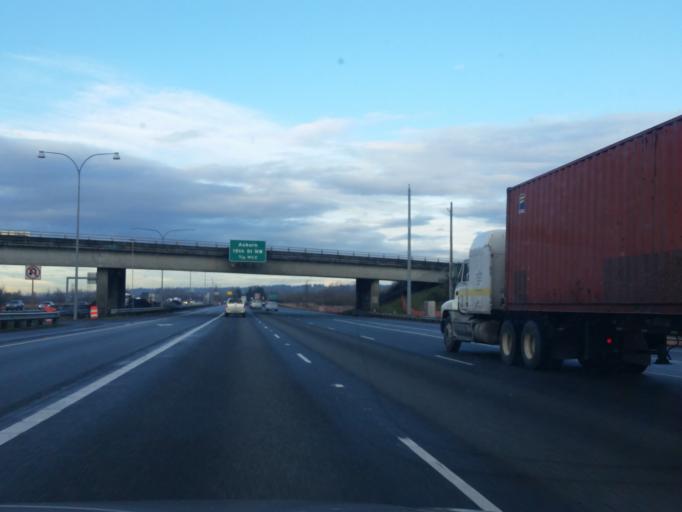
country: US
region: Washington
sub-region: King County
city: Auburn
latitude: 47.3076
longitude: -122.2490
